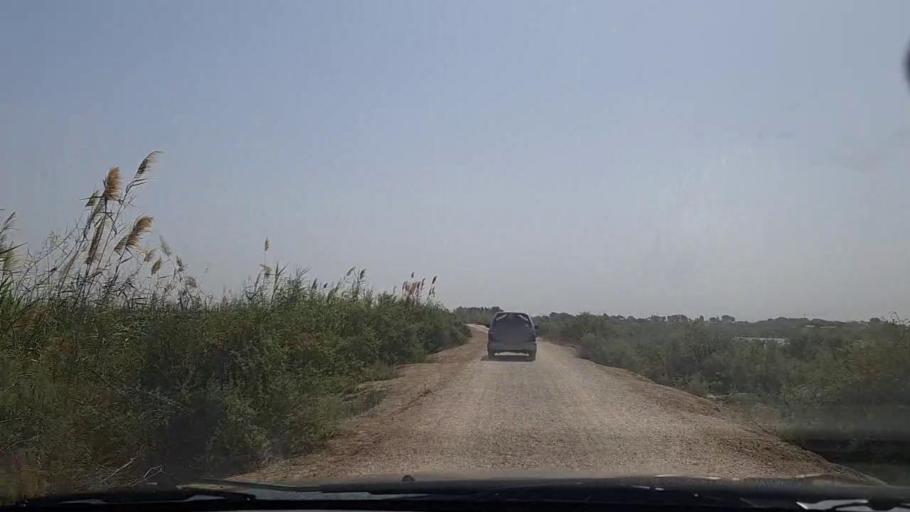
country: PK
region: Sindh
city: Mirpur Sakro
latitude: 24.3244
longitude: 67.6841
